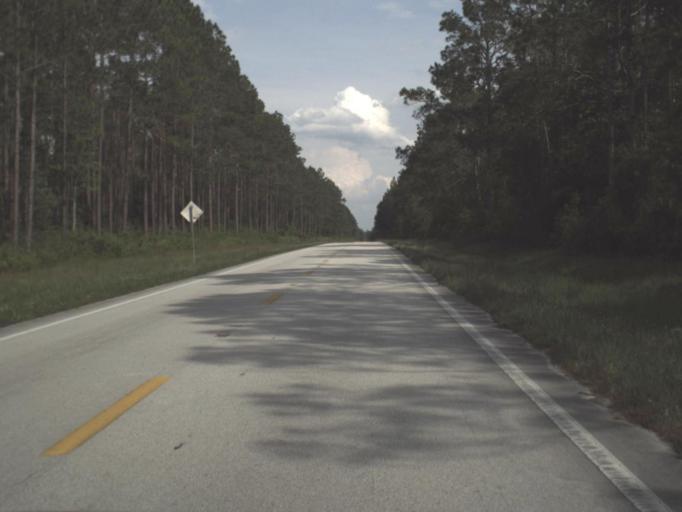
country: US
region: Florida
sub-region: Columbia County
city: Five Points
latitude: 30.5830
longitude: -82.4673
